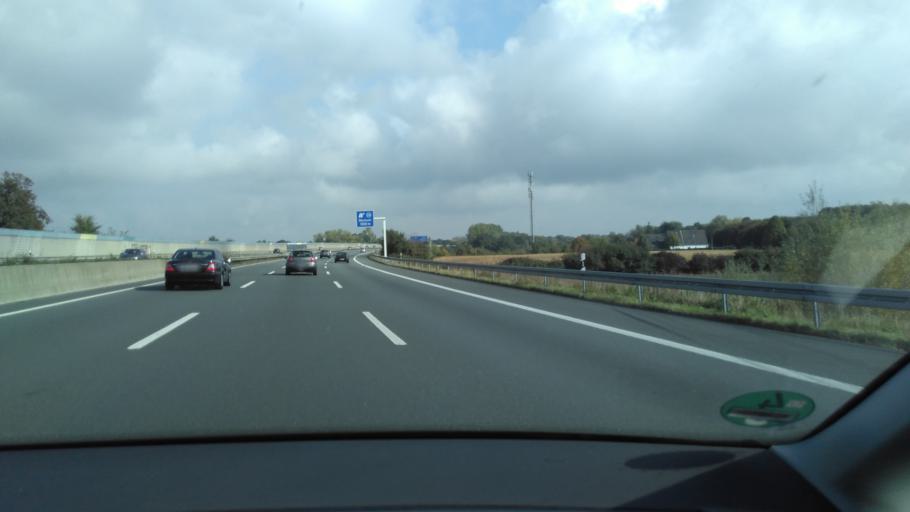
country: DE
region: North Rhine-Westphalia
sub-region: Regierungsbezirk Munster
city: Beckum
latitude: 51.7726
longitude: 8.0119
